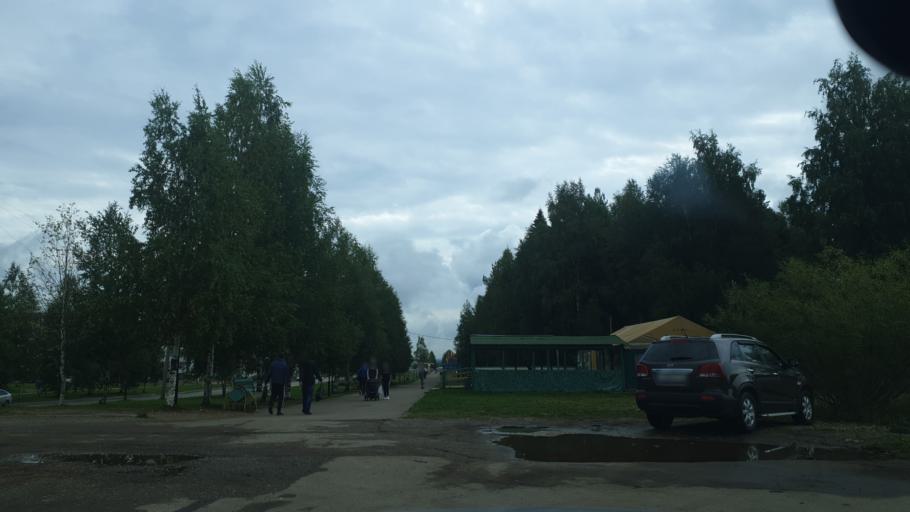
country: RU
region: Komi Republic
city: Ezhva
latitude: 61.7811
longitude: 50.7488
